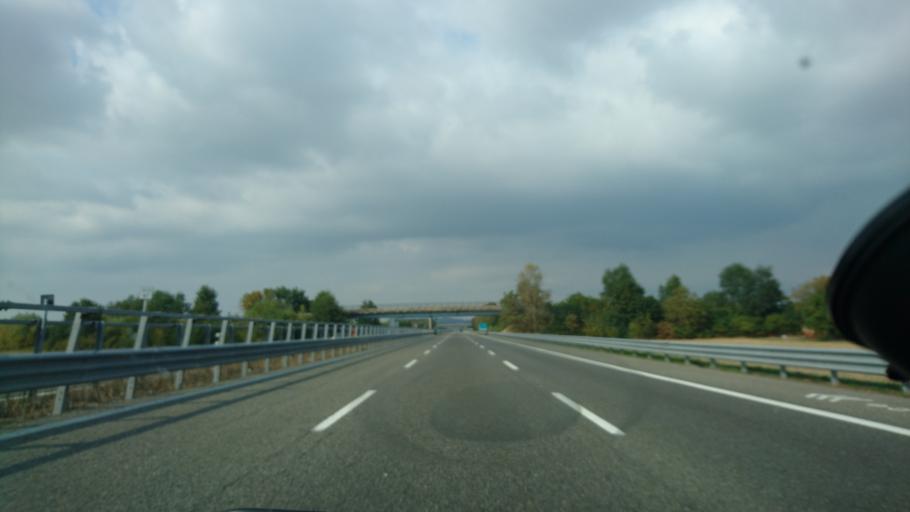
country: IT
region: Piedmont
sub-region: Provincia di Alessandria
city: Castelletto Monferrato
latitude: 44.9445
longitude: 8.5669
